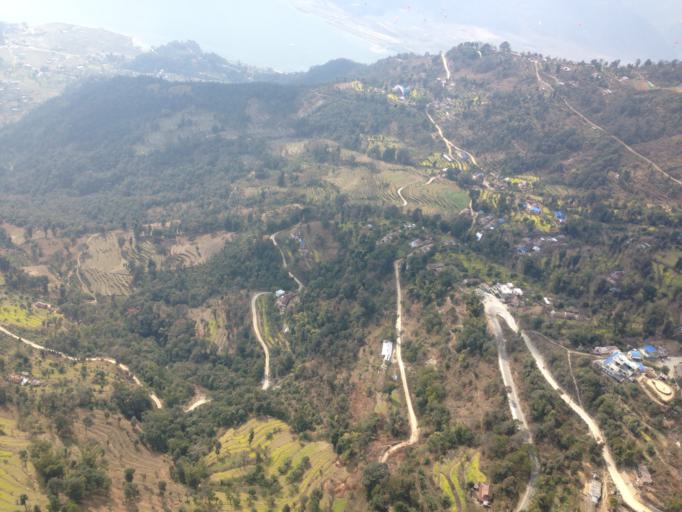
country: NP
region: Western Region
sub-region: Gandaki Zone
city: Pokhara
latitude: 28.2445
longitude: 83.9611
